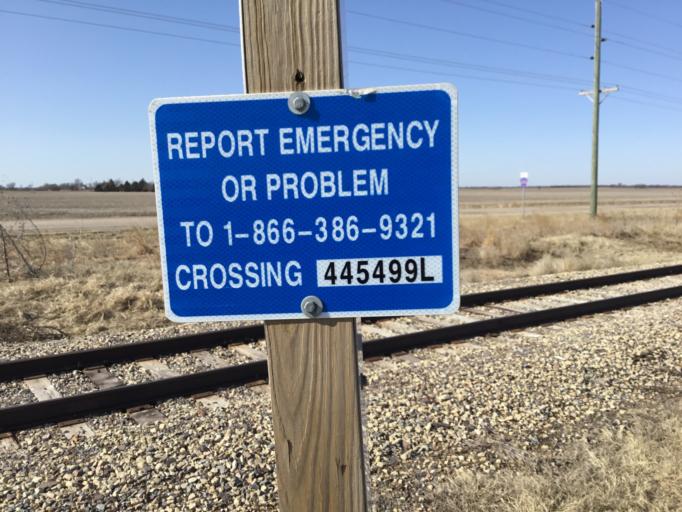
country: US
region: Kansas
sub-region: McPherson County
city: Moundridge
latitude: 38.2632
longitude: -97.5931
